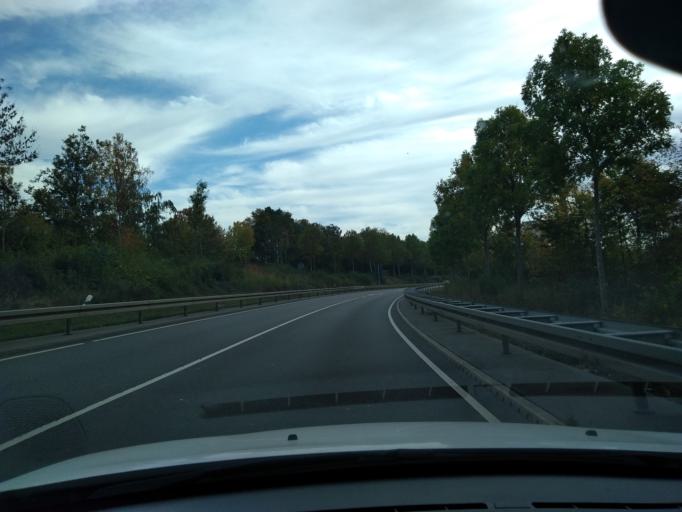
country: DE
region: Saarland
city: Ensdorf
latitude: 49.3043
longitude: 6.7722
